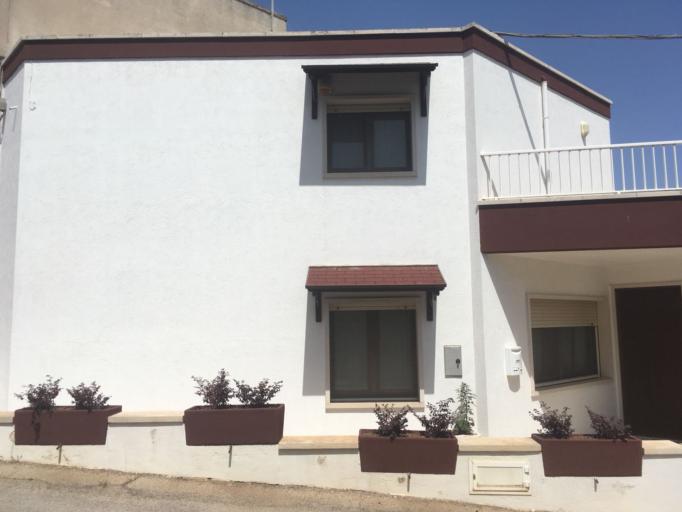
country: IT
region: Apulia
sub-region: Provincia di Brindisi
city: Casalini
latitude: 40.7381
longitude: 17.4729
